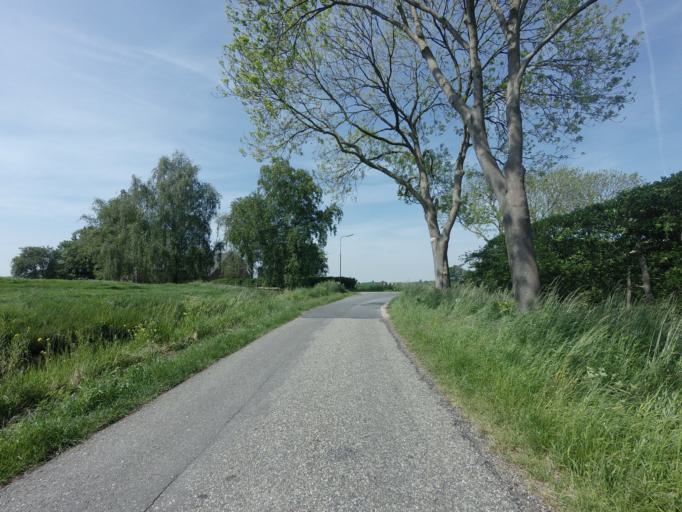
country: NL
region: Utrecht
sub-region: Gemeente De Ronde Venen
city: Mijdrecht
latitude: 52.2291
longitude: 4.8851
